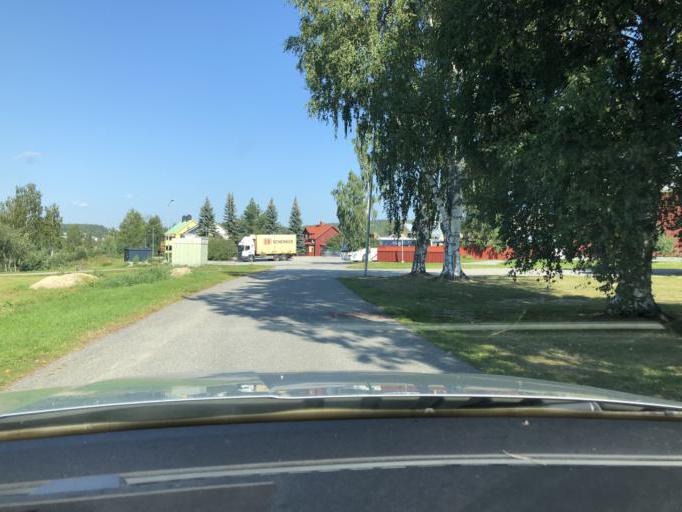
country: SE
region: Vaesternorrland
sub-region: OErnskoeldsviks Kommun
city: Bredbyn
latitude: 63.4481
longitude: 18.1057
